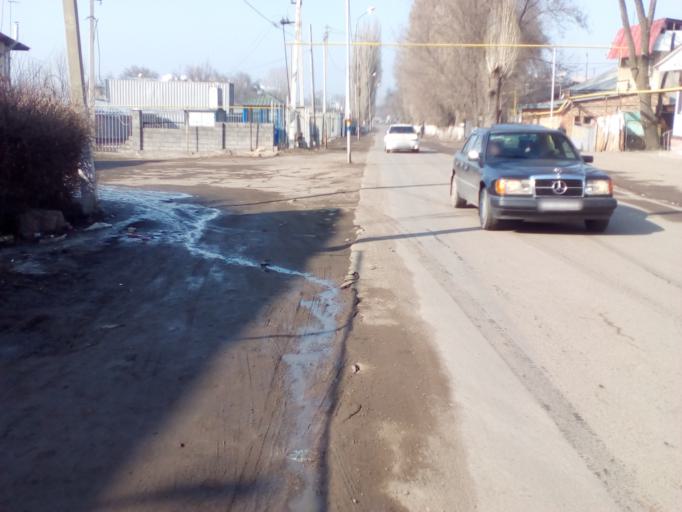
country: KZ
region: Almaty Oblysy
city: Burunday
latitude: 43.1583
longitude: 76.4140
